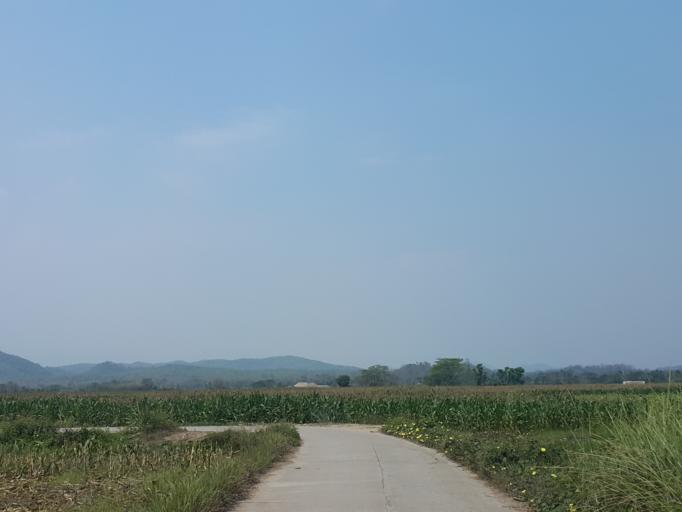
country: TH
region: Lampang
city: Chae Hom
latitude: 18.7467
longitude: 99.5635
